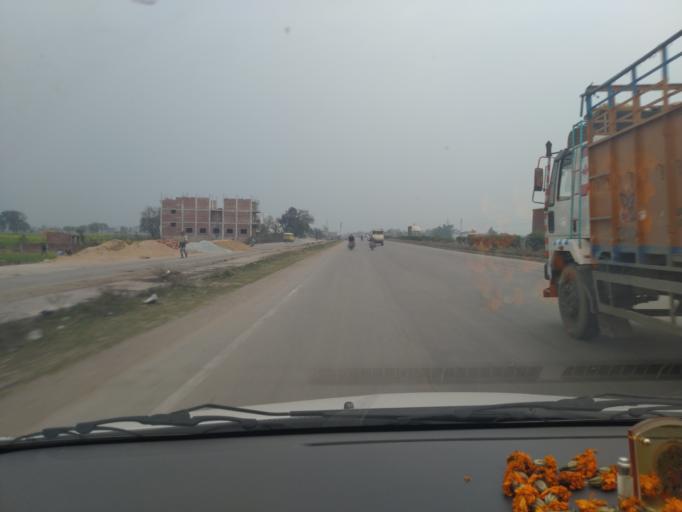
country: IN
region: Bihar
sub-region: Rohtas
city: Dehri
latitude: 24.9740
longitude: 83.9061
